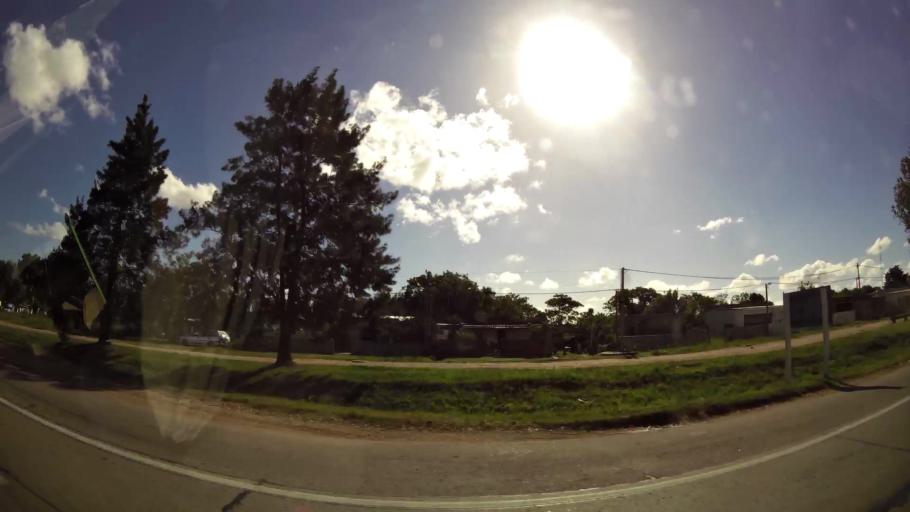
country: UY
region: Montevideo
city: Montevideo
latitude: -34.8607
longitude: -56.2567
